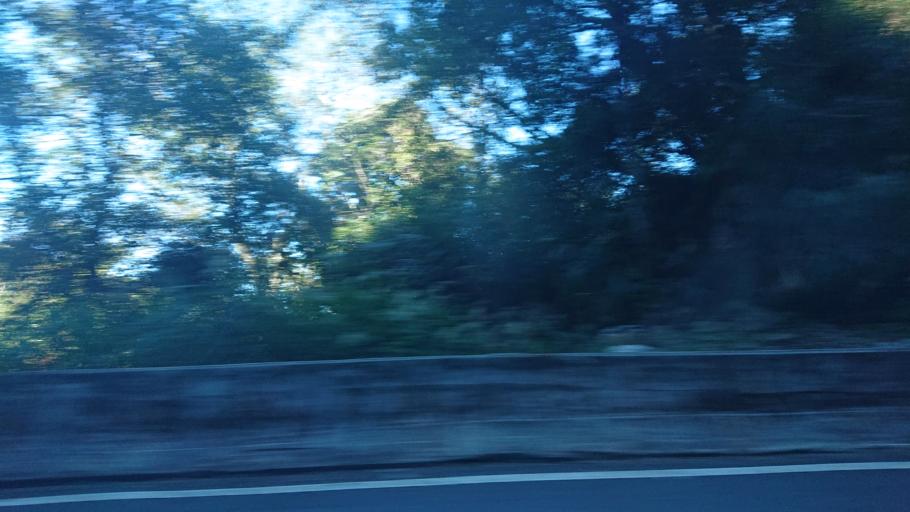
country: TW
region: Taiwan
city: Lugu
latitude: 23.4790
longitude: 120.8526
